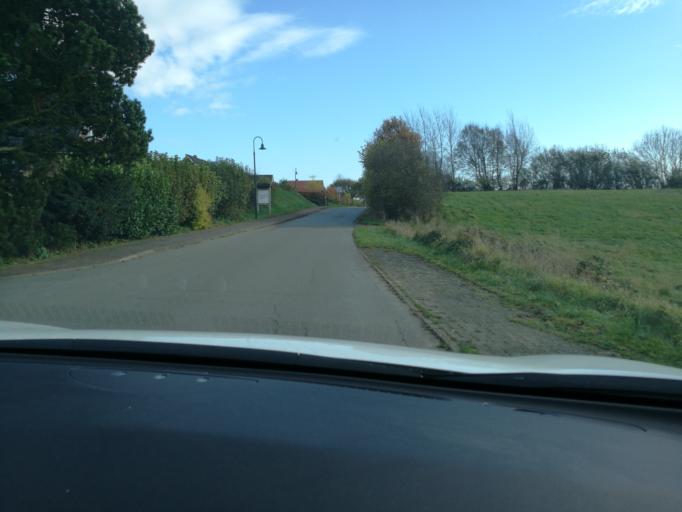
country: DE
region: Schleswig-Holstein
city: Bunsdorf
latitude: 54.3694
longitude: 9.7482
